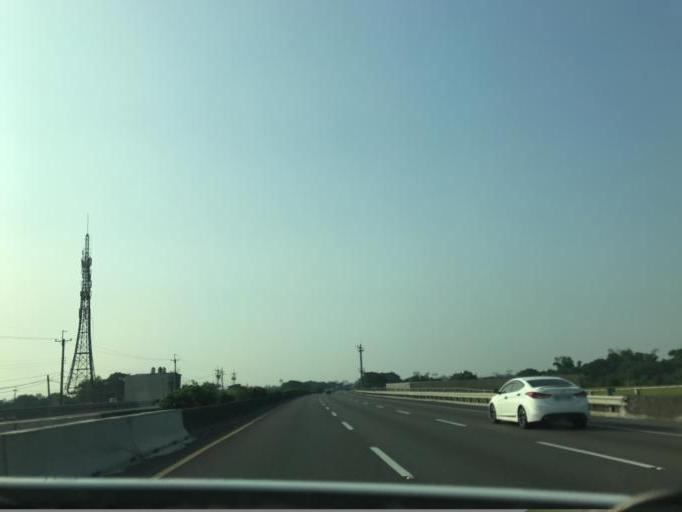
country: TW
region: Taiwan
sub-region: Chiayi
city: Jiayi Shi
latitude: 23.5143
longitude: 120.4036
